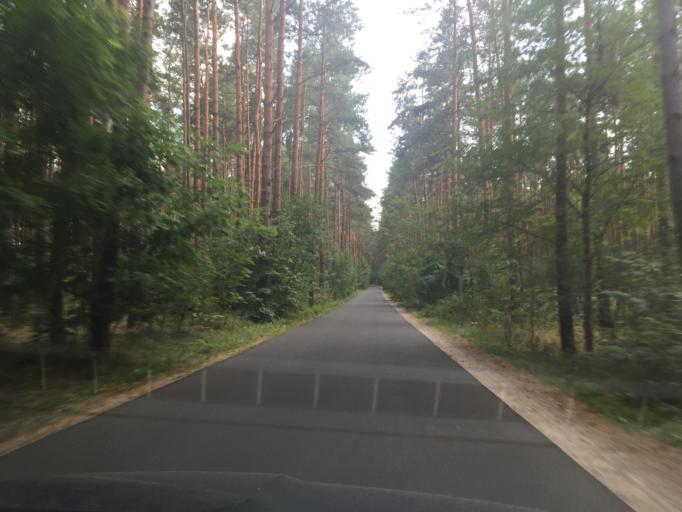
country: DE
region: Brandenburg
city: Grunheide
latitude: 52.3675
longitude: 13.7882
